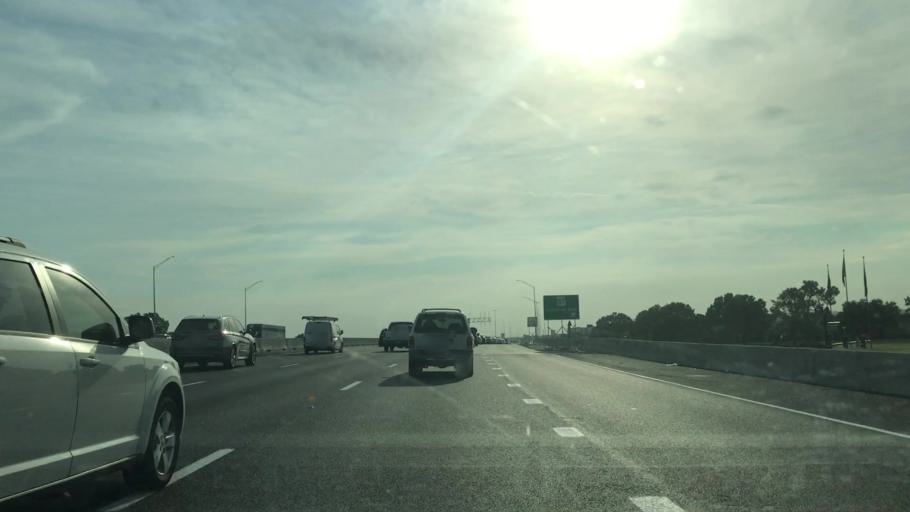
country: US
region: Texas
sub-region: Tarrant County
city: Euless
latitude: 32.8384
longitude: -97.0893
